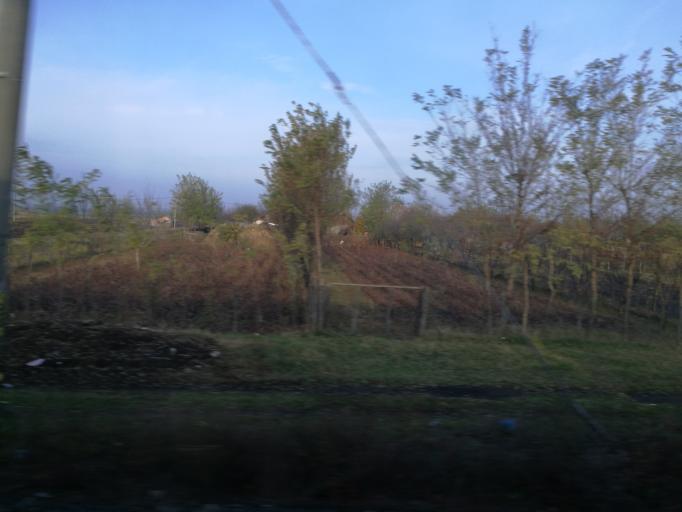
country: RO
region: Buzau
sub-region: Comuna Cochirleanca
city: Cochirleanca
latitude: 45.2754
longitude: 27.0051
